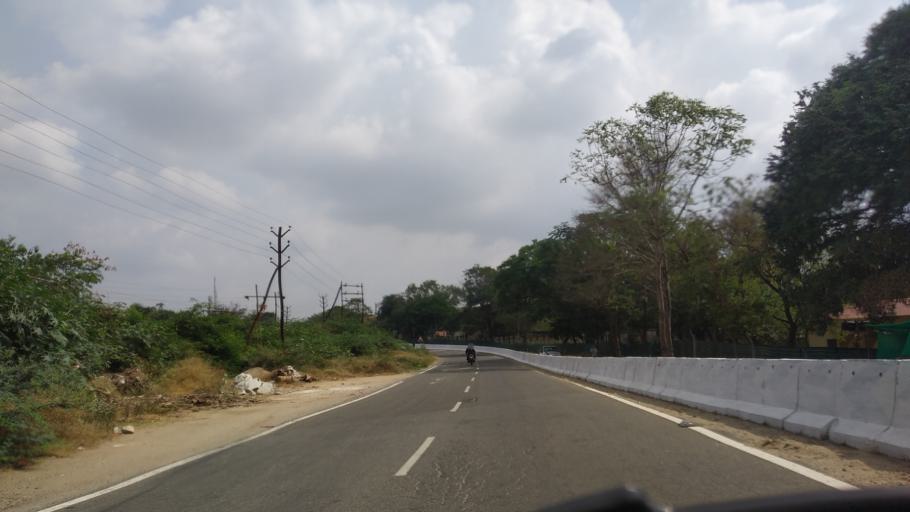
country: IN
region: Tamil Nadu
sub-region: Coimbatore
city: Madukkarai
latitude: 10.9044
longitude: 76.9443
